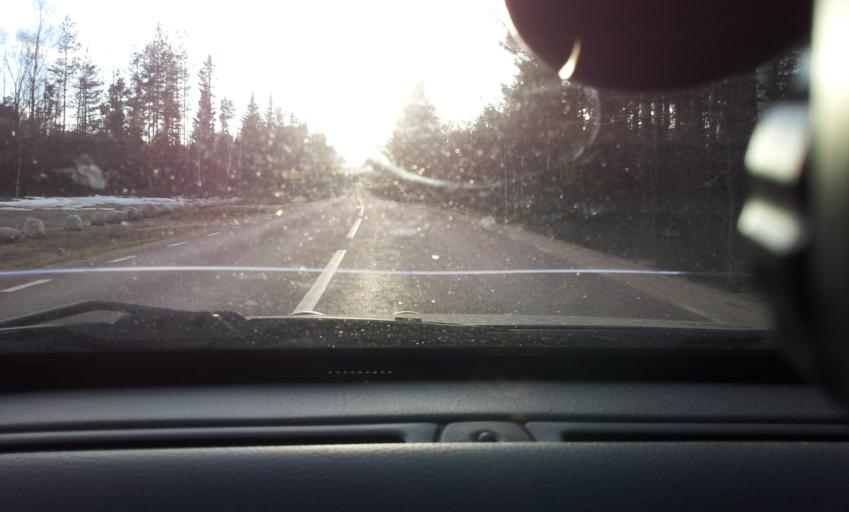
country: SE
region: Jaemtland
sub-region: Harjedalens Kommun
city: Sveg
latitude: 62.1785
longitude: 14.9060
